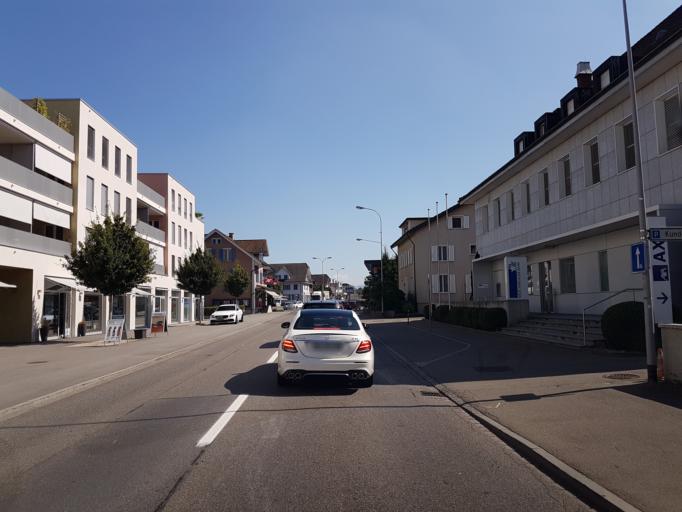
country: CH
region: Aargau
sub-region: Bezirk Muri
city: Muri
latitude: 47.2745
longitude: 8.3409
